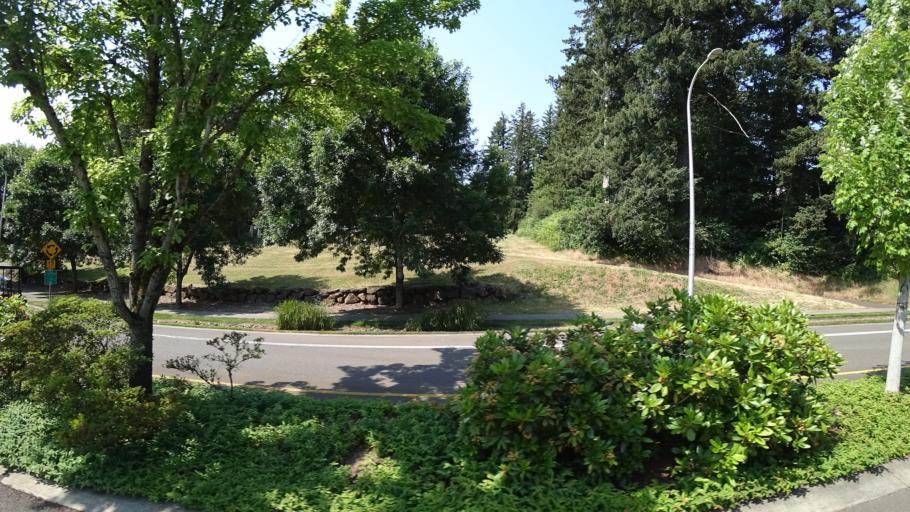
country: US
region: Oregon
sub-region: Clackamas County
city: Happy Valley
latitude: 45.4400
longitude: -122.5540
